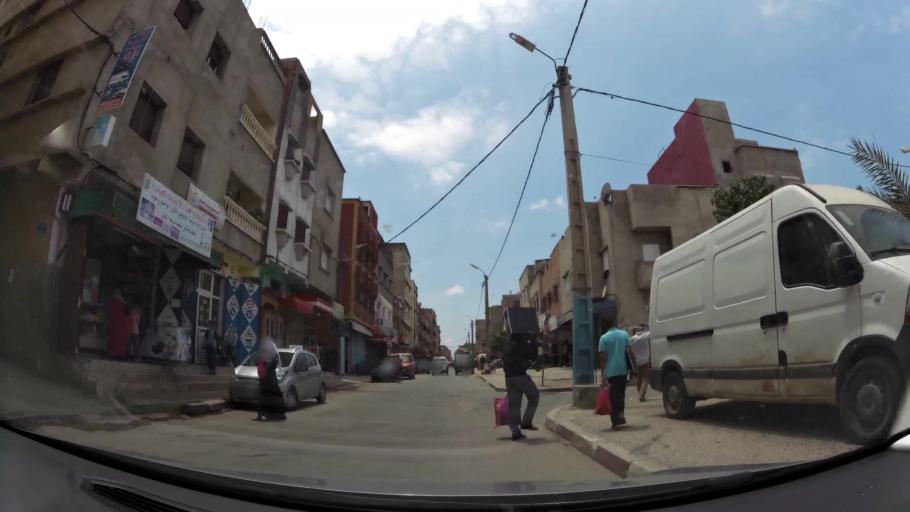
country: MA
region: Rabat-Sale-Zemmour-Zaer
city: Sale
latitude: 34.0670
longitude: -6.7708
